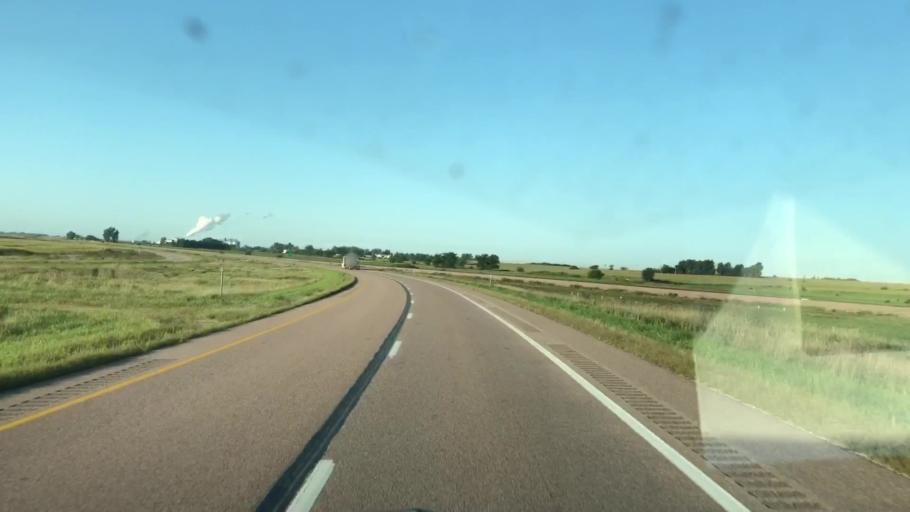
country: US
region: Iowa
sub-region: Osceola County
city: Sibley
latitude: 43.3003
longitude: -95.7914
